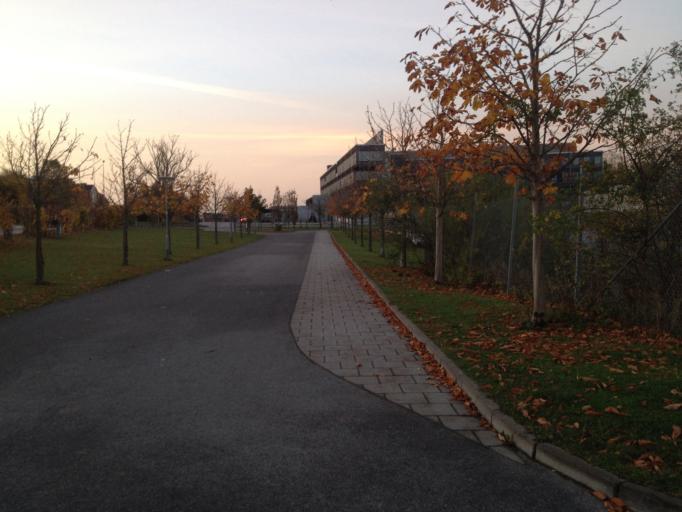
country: SE
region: Skane
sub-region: Lunds Kommun
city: Lund
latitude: 55.7166
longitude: 13.2131
